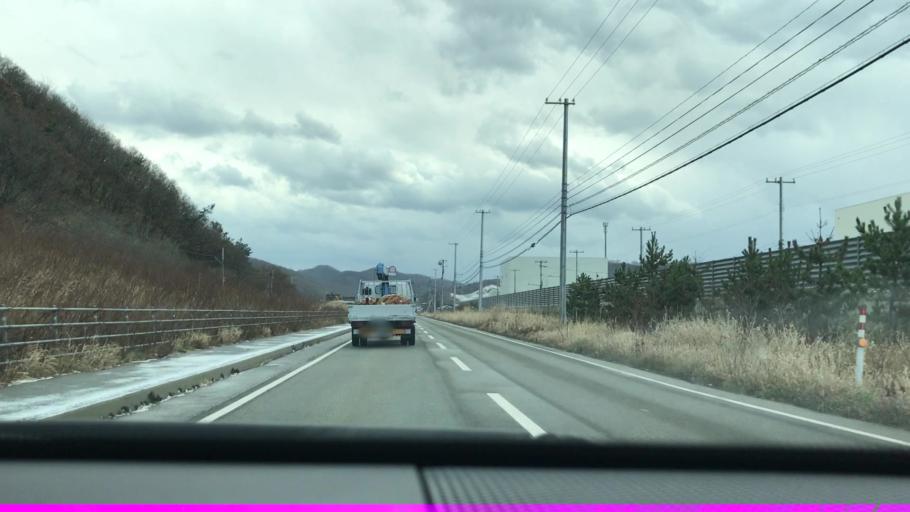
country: JP
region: Hokkaido
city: Shizunai-furukawacho
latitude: 42.3060
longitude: 142.4443
